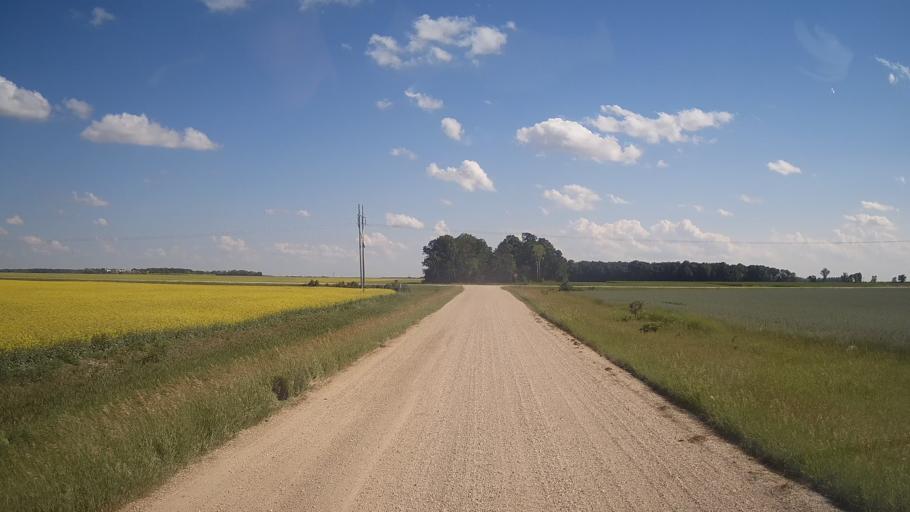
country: CA
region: Manitoba
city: Stonewall
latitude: 50.1244
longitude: -97.5054
